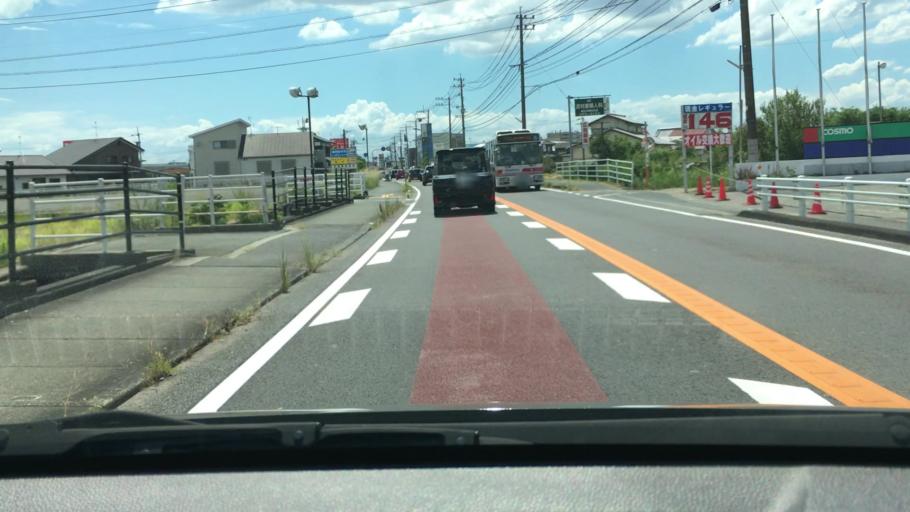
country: JP
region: Saga Prefecture
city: Kanzakimachi-kanzaki
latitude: 33.3186
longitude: 130.3824
